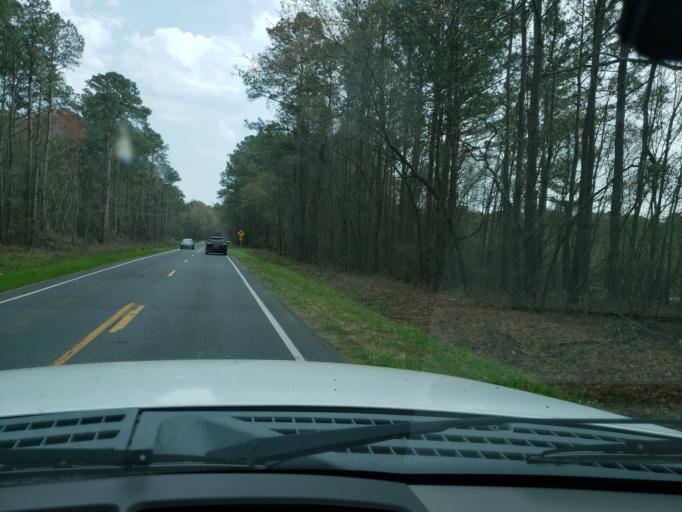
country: US
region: North Carolina
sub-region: Duplin County
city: Beulaville
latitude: 34.7893
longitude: -77.8425
